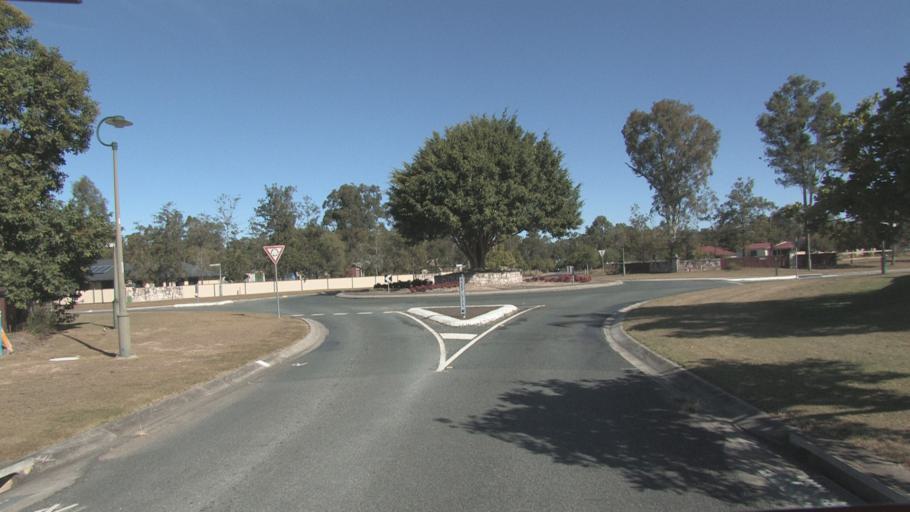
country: AU
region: Queensland
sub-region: Logan
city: North Maclean
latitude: -27.8016
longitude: 152.9675
